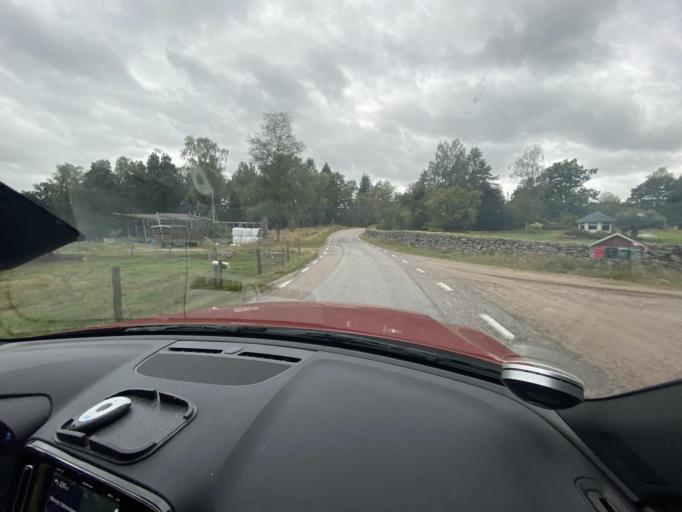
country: SE
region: Kronoberg
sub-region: Markaryds Kommun
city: Markaryd
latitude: 56.4977
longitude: 13.5308
